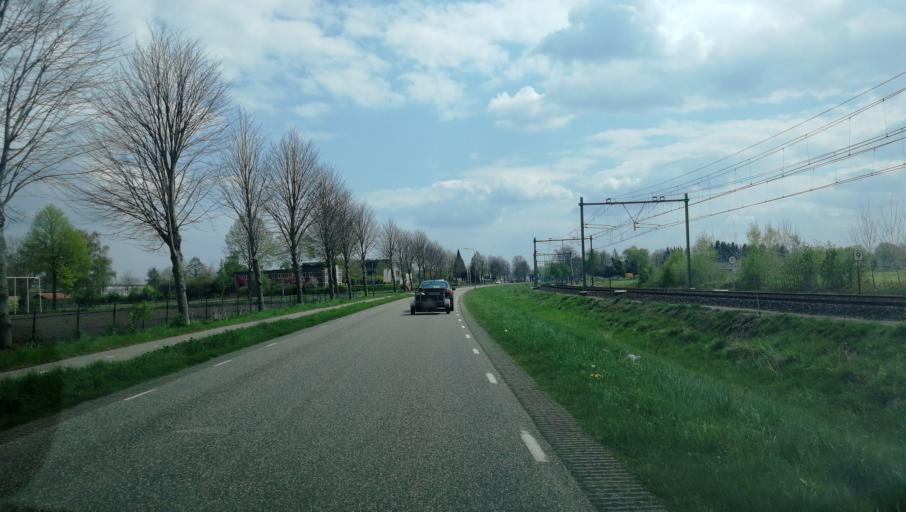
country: NL
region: Limburg
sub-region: Gemeente Peel en Maas
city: Maasbree
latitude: 51.4302
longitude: 6.0330
